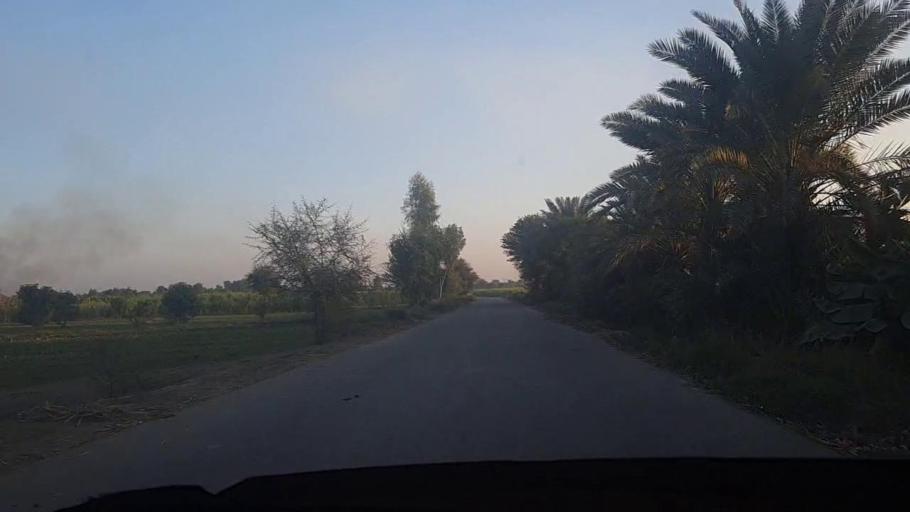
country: PK
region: Sindh
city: Sobhadero
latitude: 27.3439
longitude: 68.3775
